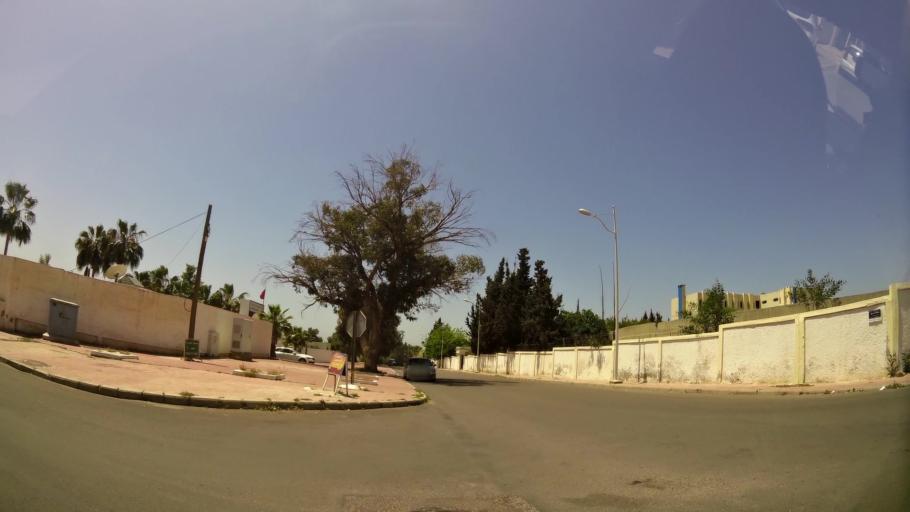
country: MA
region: Souss-Massa-Draa
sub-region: Agadir-Ida-ou-Tnan
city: Agadir
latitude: 30.4352
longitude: -9.5851
